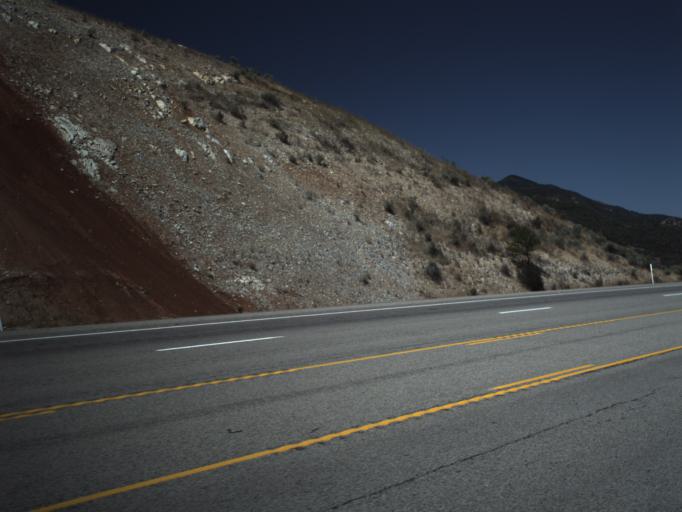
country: US
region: Utah
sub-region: Utah County
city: Mapleton
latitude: 40.0033
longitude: -111.4909
